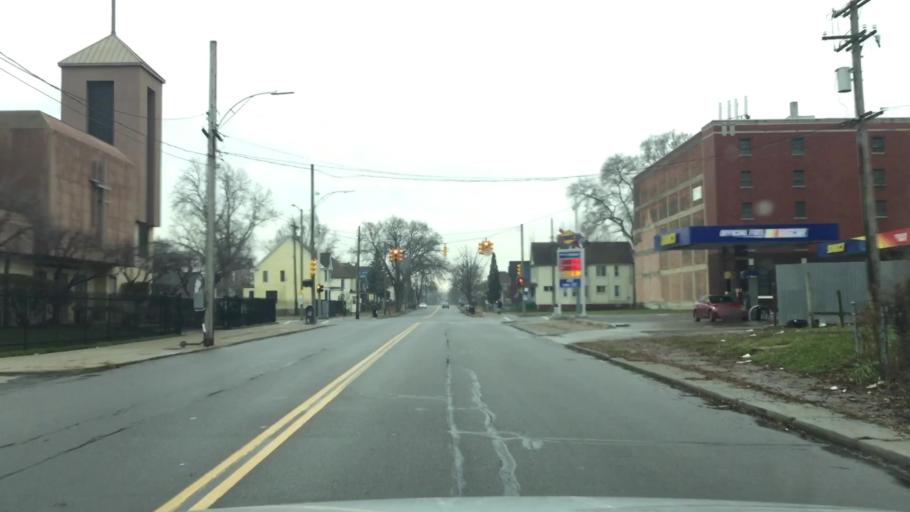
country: US
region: Michigan
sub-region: Wayne County
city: Hamtramck
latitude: 42.3675
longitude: -83.0066
